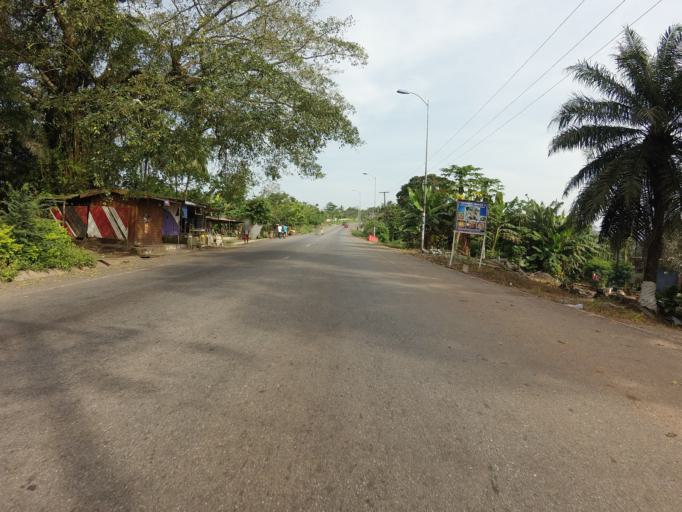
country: GH
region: Eastern
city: Aburi
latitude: 5.8209
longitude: -0.1863
